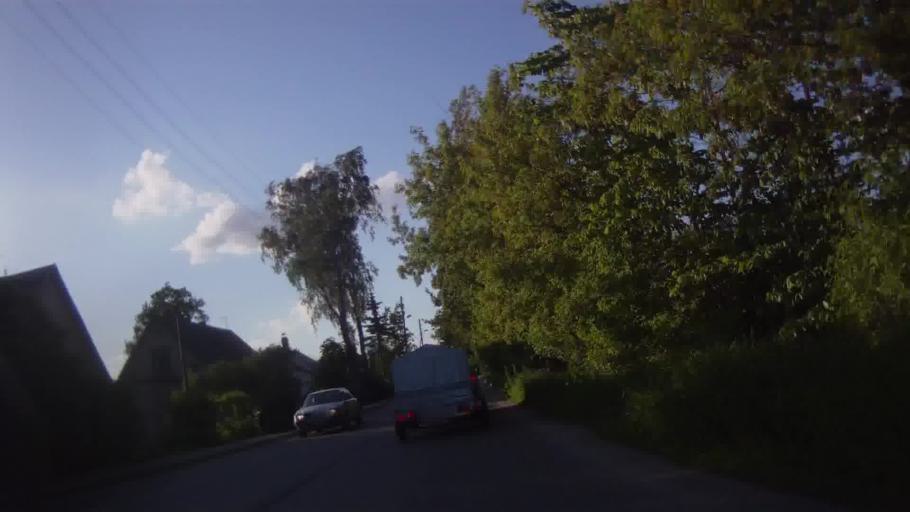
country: LV
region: Rezekne
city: Rezekne
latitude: 56.5172
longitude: 27.3219
